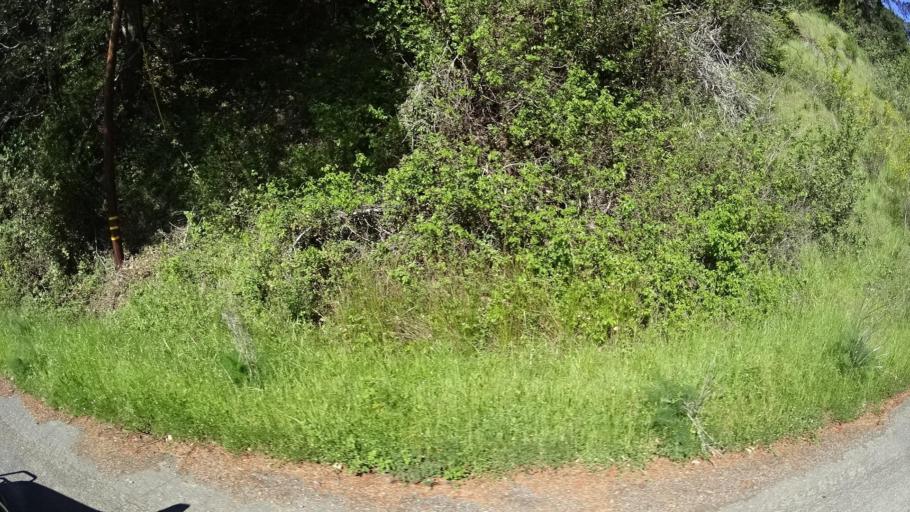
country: US
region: California
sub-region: Humboldt County
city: Rio Dell
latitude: 40.2651
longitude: -124.1970
